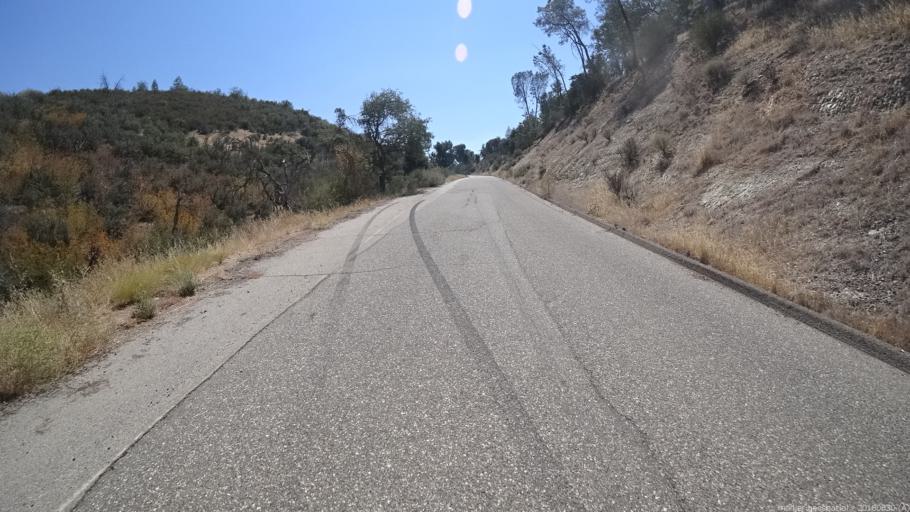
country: US
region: California
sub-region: Monterey County
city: King City
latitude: 35.9961
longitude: -121.2614
